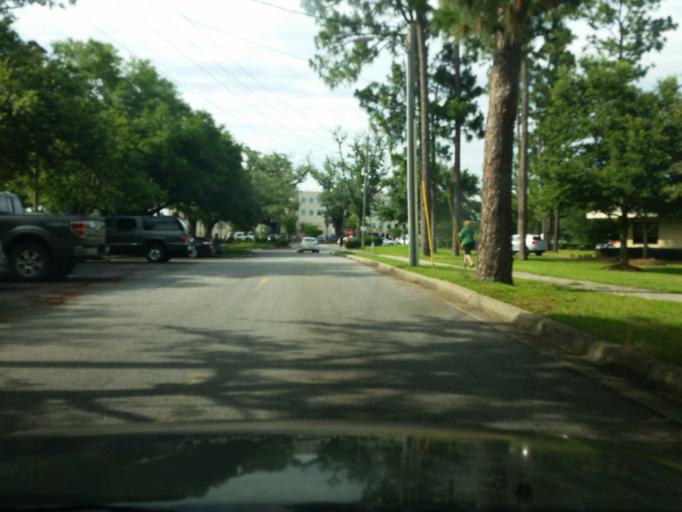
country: US
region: Florida
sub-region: Escambia County
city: Brent
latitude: 30.4788
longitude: -87.2115
